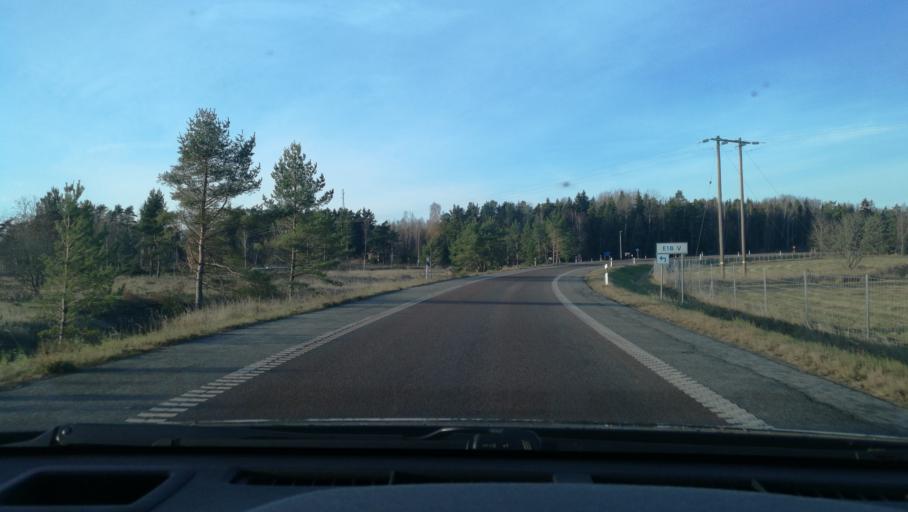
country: SE
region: Vaestmanland
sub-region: Hallstahammars Kommun
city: Kolback
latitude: 59.5926
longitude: 16.2511
